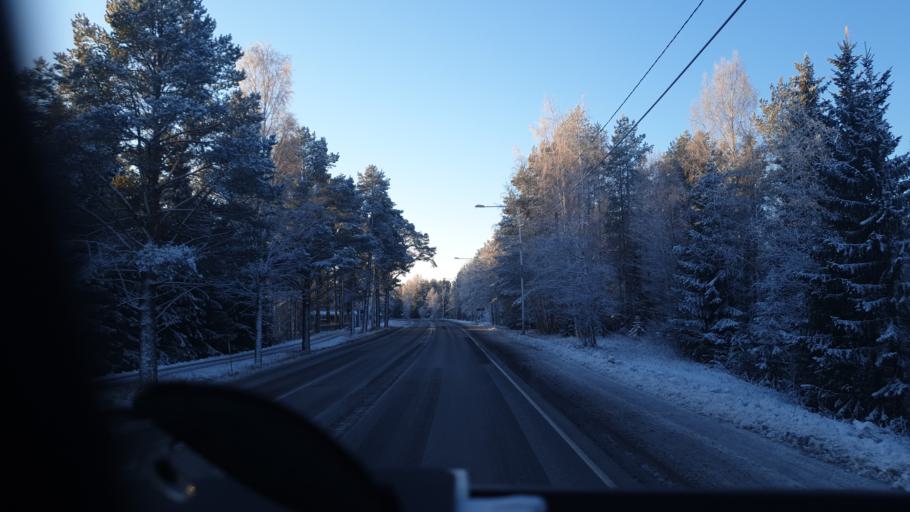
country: FI
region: Northern Ostrobothnia
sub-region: Ylivieska
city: Himanka
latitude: 64.2080
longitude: 23.7673
